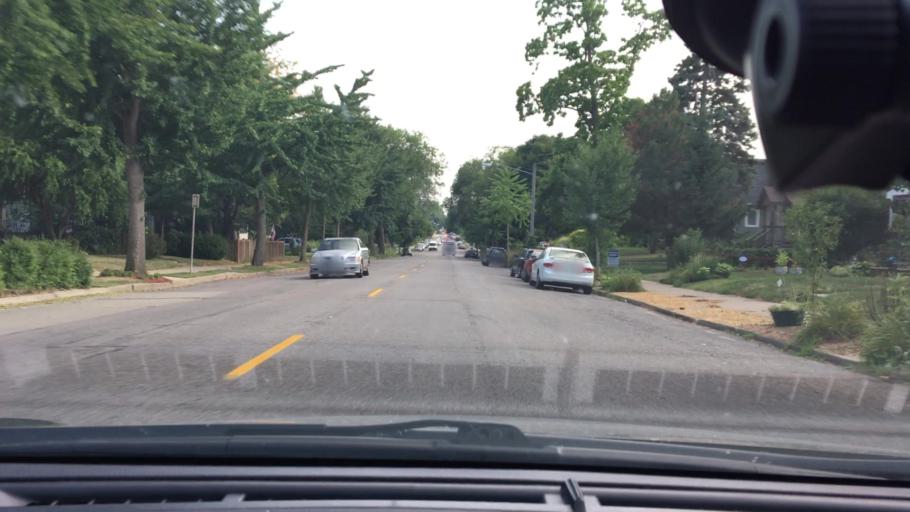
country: US
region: Minnesota
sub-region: Hennepin County
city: Minneapolis
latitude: 44.9322
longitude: -93.2524
